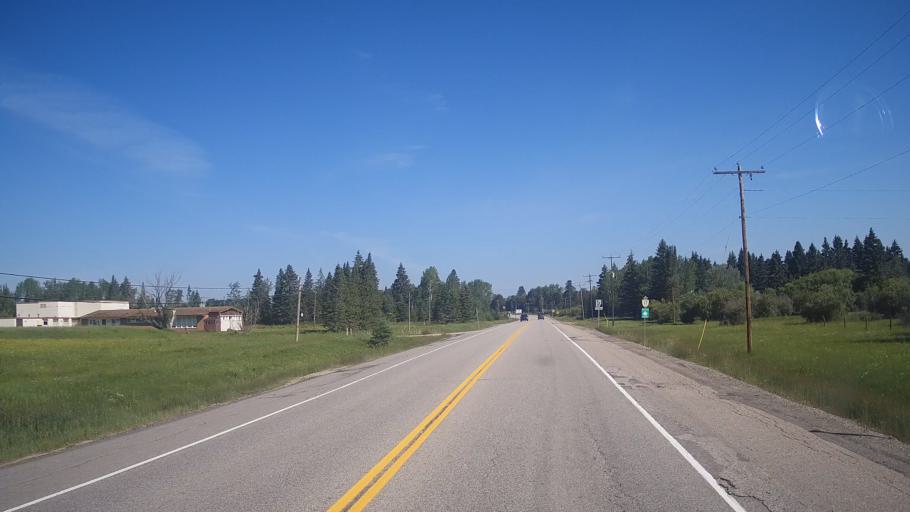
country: CA
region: Ontario
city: Dryden
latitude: 49.7279
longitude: -92.6087
